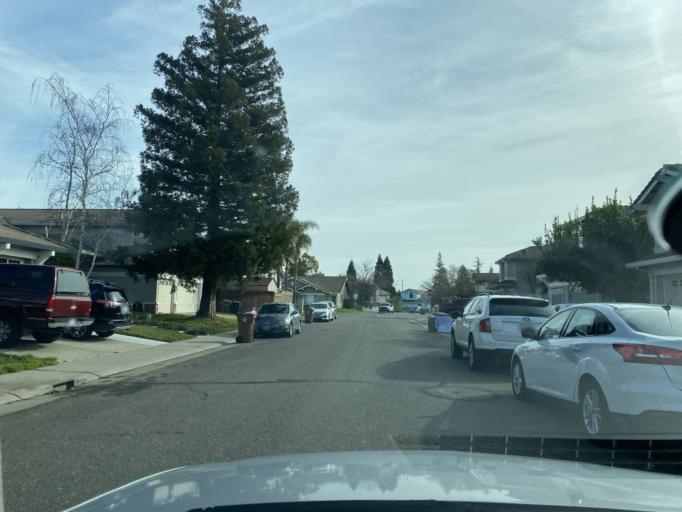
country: US
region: California
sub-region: Sacramento County
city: Elk Grove
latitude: 38.4357
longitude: -121.3774
